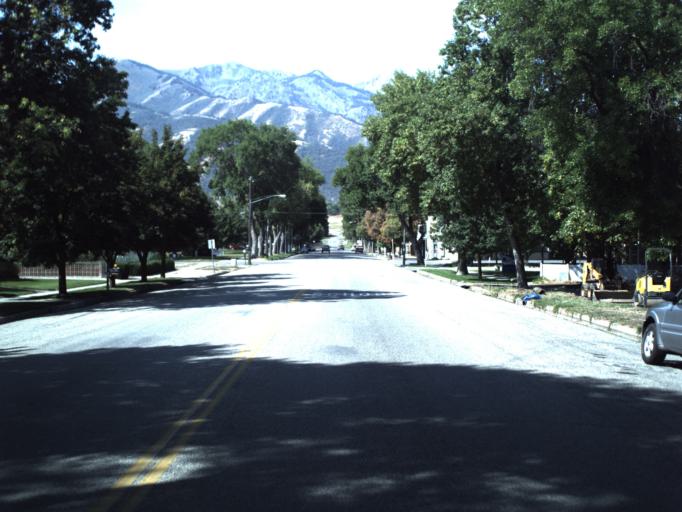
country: US
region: Utah
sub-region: Cache County
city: Wellsville
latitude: 41.6387
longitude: -111.9301
